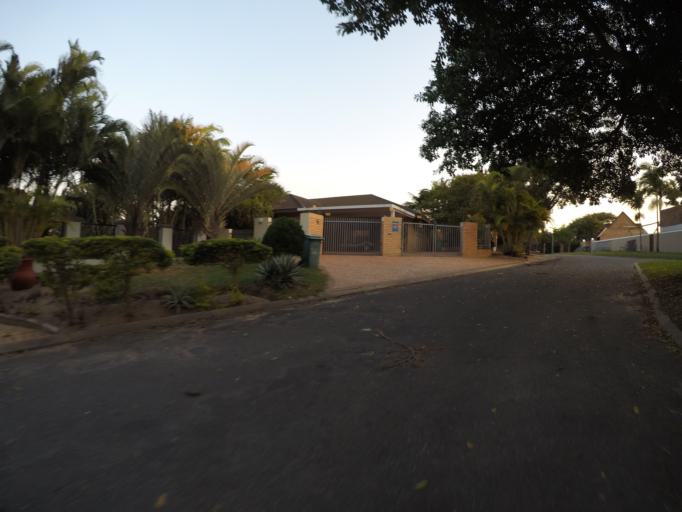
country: ZA
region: KwaZulu-Natal
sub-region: uThungulu District Municipality
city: Richards Bay
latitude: -28.7670
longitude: 32.1233
